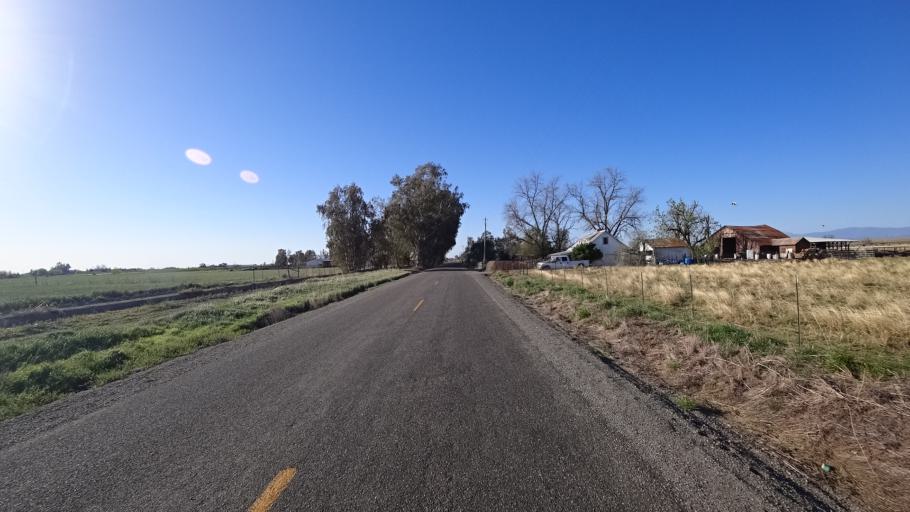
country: US
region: California
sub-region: Glenn County
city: Orland
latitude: 39.7574
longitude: -122.2479
